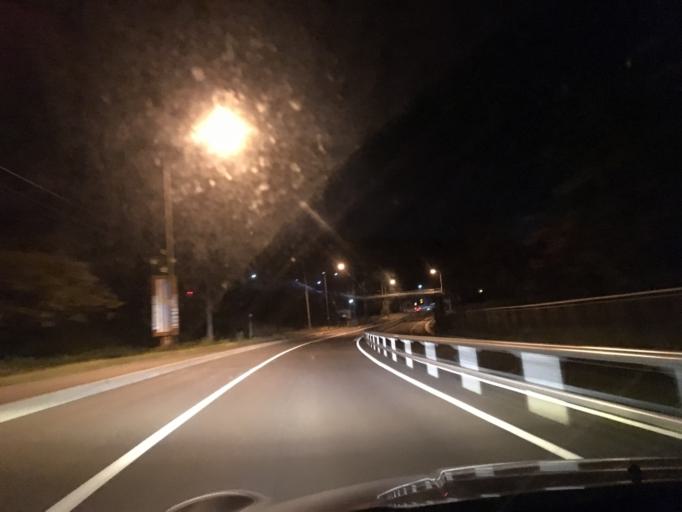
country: JP
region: Hokkaido
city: Muroran
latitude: 42.3626
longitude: 140.9630
